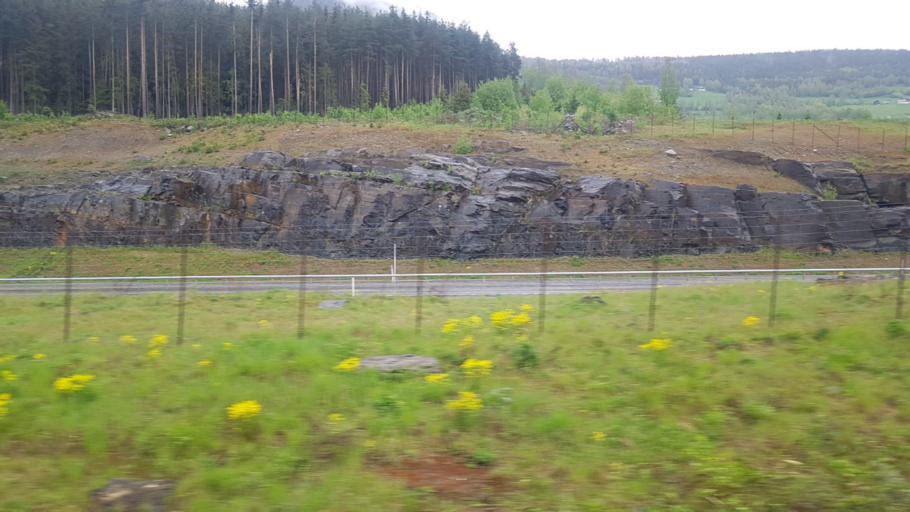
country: NO
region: Oppland
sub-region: Sor-Fron
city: Hundorp
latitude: 61.5709
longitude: 9.8672
